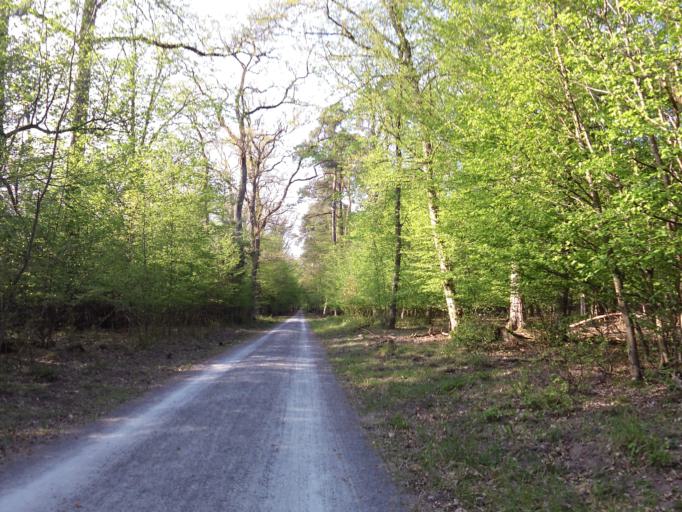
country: DE
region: Hesse
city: Raunheim
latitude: 49.9946
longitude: 8.5118
